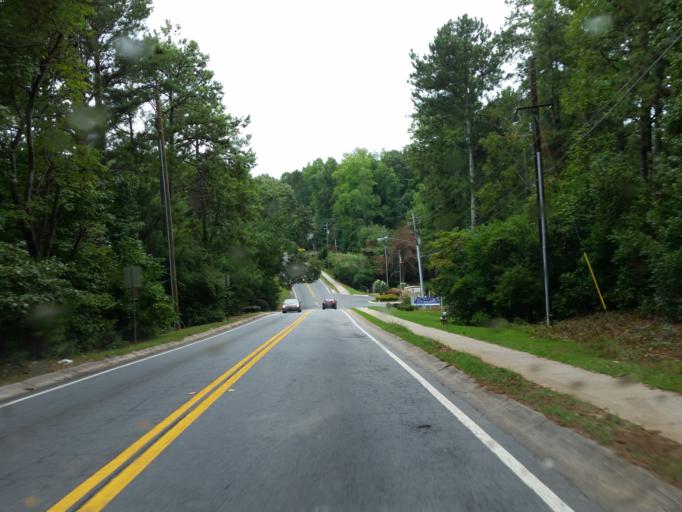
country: US
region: Georgia
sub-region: Cobb County
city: Smyrna
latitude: 33.9190
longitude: -84.4760
